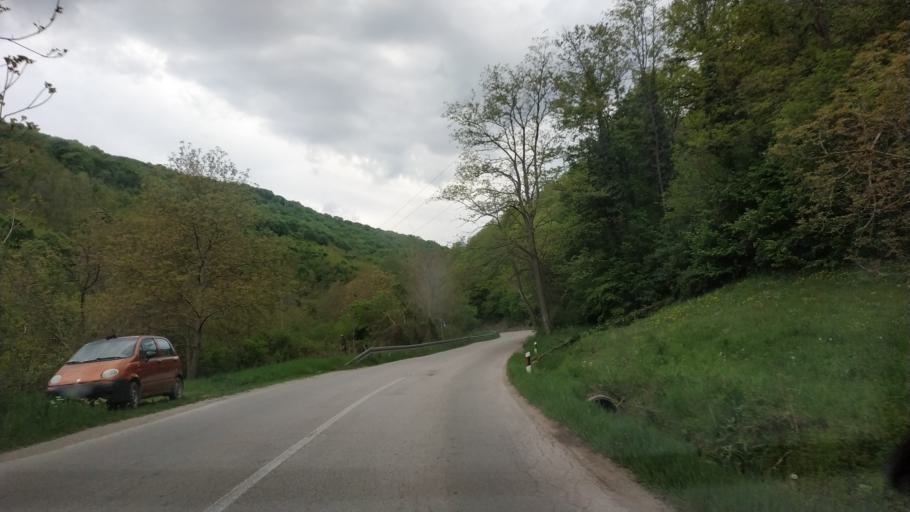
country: RS
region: Central Serbia
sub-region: Nisavski Okrug
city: Aleksinac
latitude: 43.6270
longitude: 21.7134
